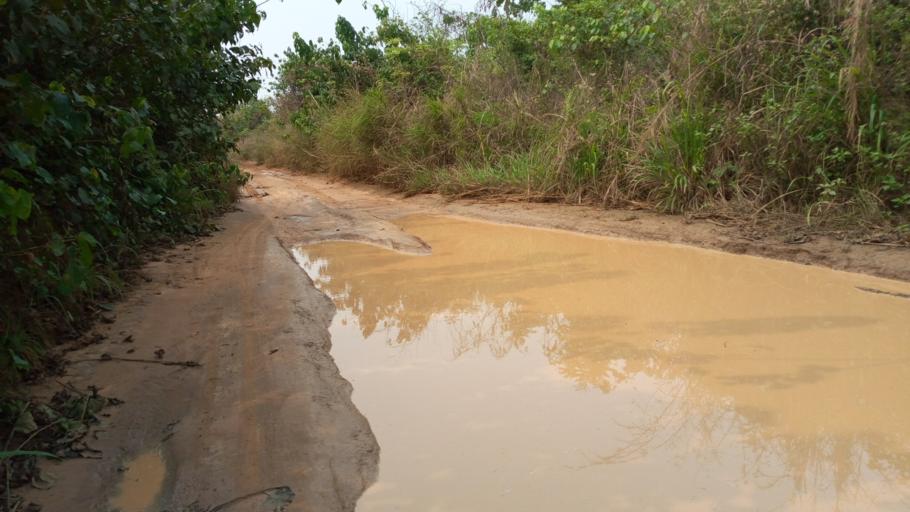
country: CD
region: Bandundu
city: Bandundu
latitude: -3.4584
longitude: 17.7693
